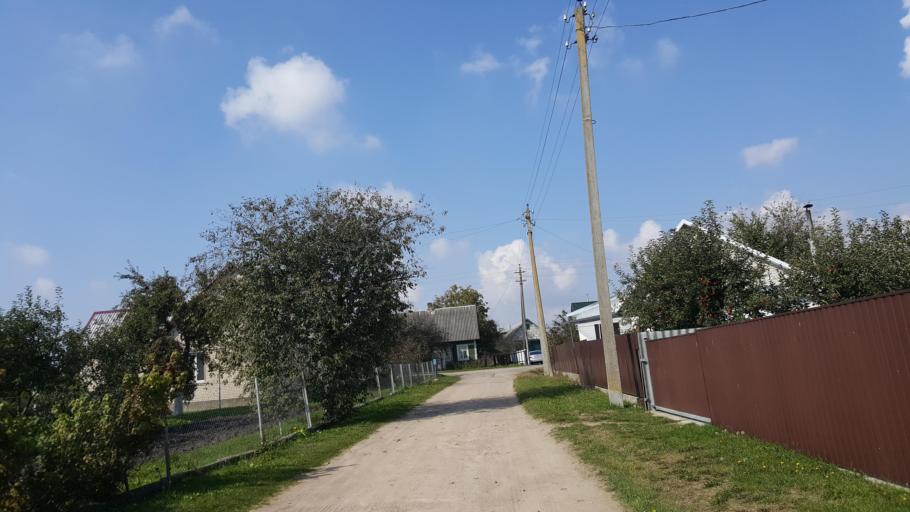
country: BY
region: Brest
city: Kamyanyets
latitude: 52.4050
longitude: 23.7976
